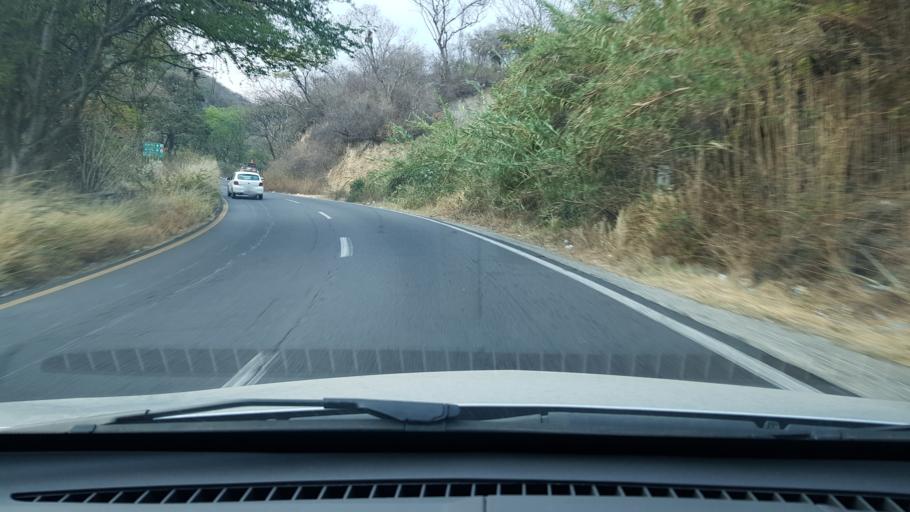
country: MX
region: Morelos
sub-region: Jiutepec
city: Independencia
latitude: 18.8739
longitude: -99.1198
